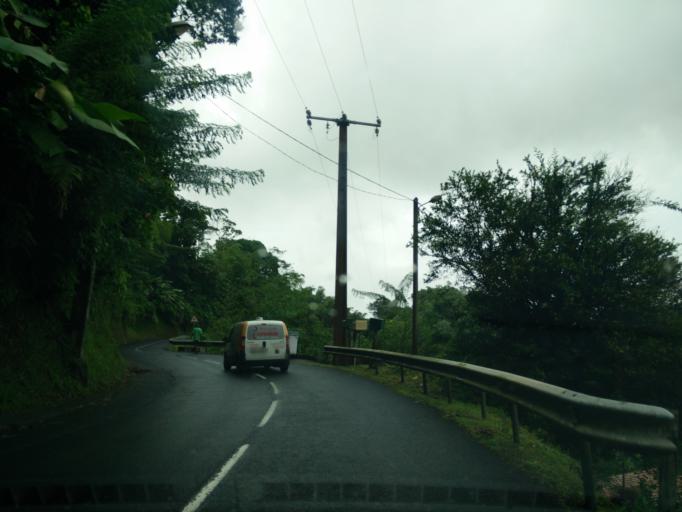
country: MQ
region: Martinique
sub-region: Martinique
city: Saint-Joseph
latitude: 14.6692
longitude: -61.0898
